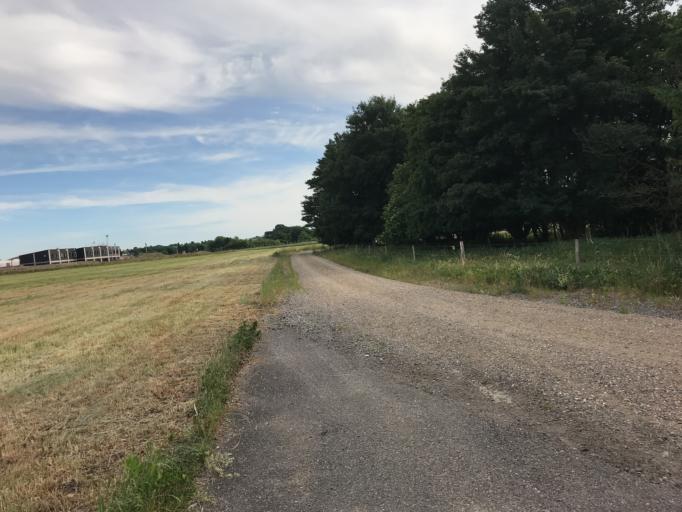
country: DK
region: Capital Region
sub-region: Ballerup Kommune
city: Malov
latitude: 55.7680
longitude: 12.3055
